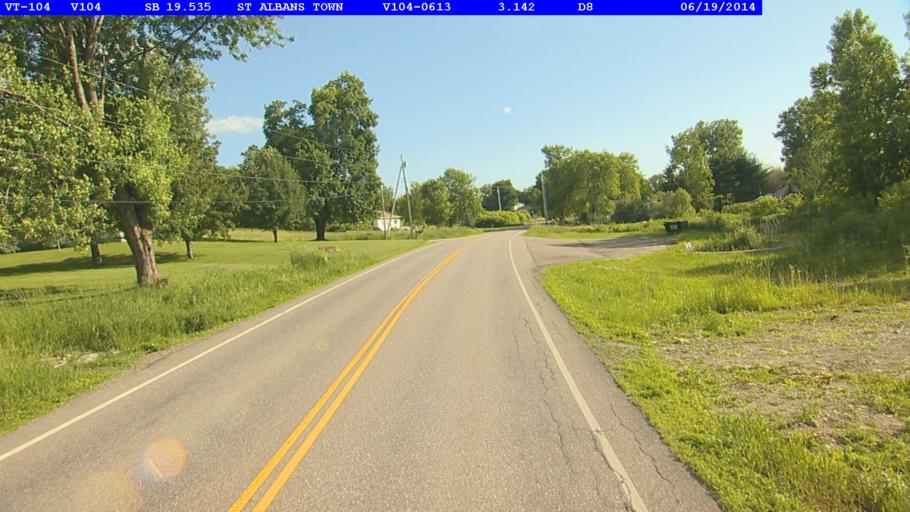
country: US
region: Vermont
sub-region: Franklin County
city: Saint Albans
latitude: 44.8158
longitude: -73.0605
